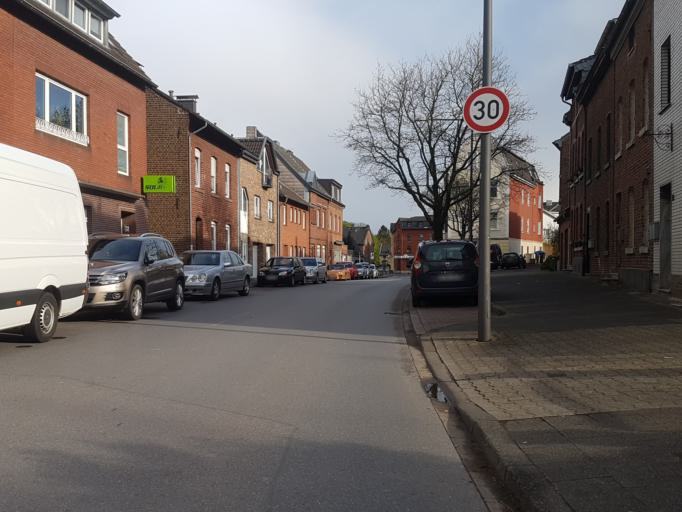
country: DE
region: North Rhine-Westphalia
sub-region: Regierungsbezirk Koln
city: Wurselen
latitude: 50.7811
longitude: 6.1619
